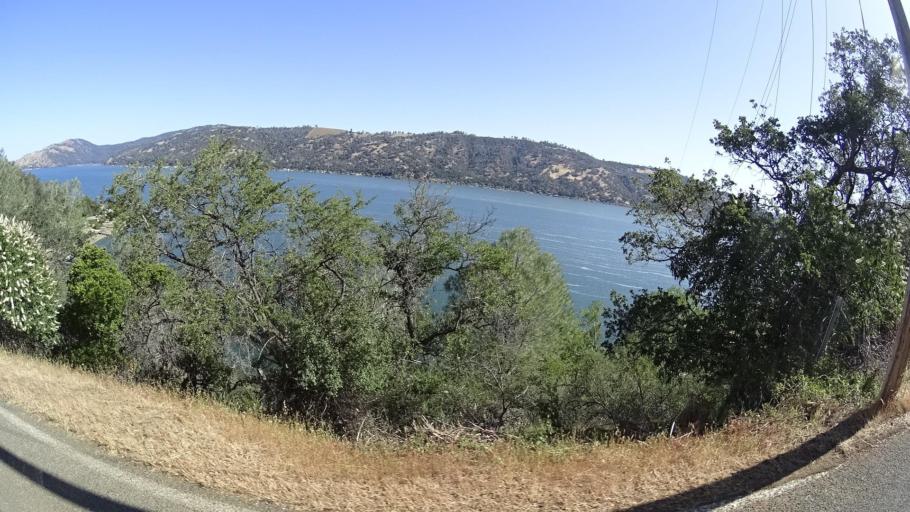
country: US
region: California
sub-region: Lake County
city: Clearlake Oaks
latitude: 39.0052
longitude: -122.7193
